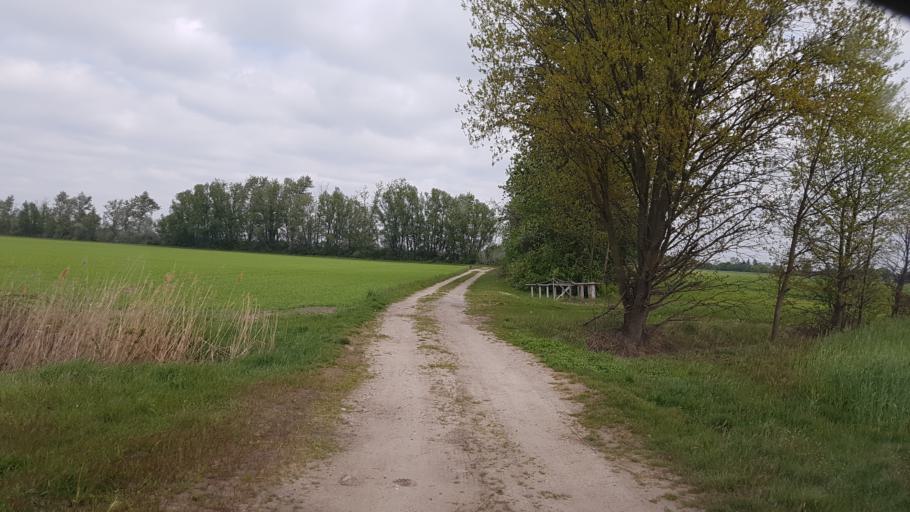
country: DE
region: Brandenburg
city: Sonnewalde
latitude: 51.6789
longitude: 13.6334
